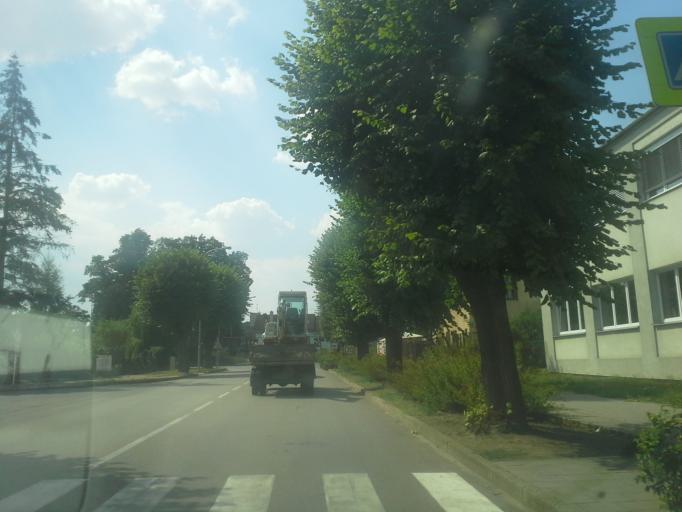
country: CZ
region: South Moravian
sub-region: Okres Blansko
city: Boskovice
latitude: 49.4923
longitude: 16.6538
